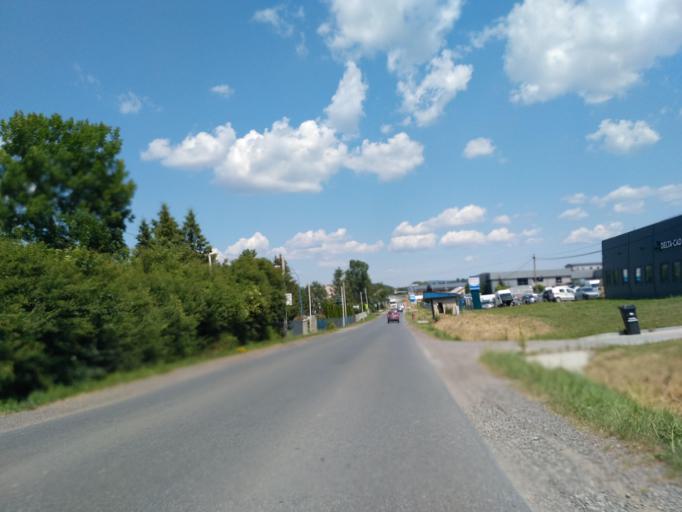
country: PL
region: Subcarpathian Voivodeship
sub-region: Powiat sanocki
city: Sanok
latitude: 49.5593
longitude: 22.1507
